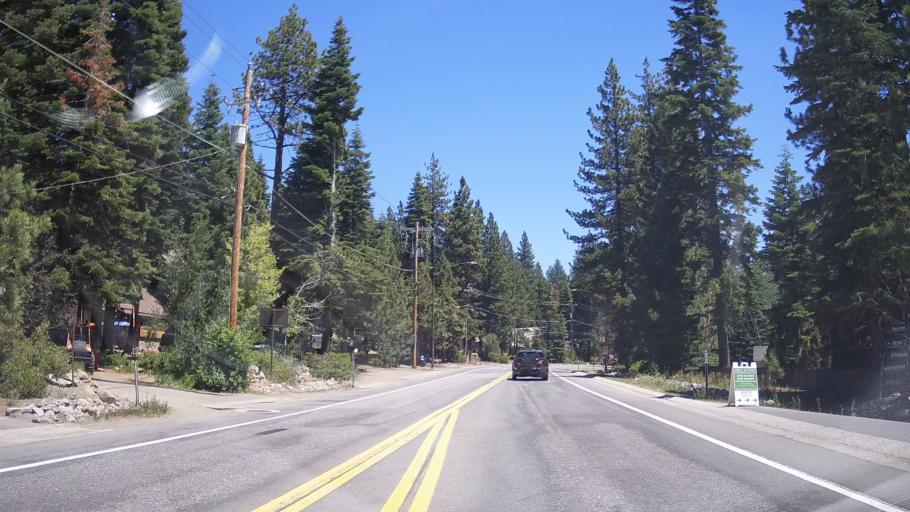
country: US
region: California
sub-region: Placer County
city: Dollar Point
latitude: 39.2078
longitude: -120.0932
